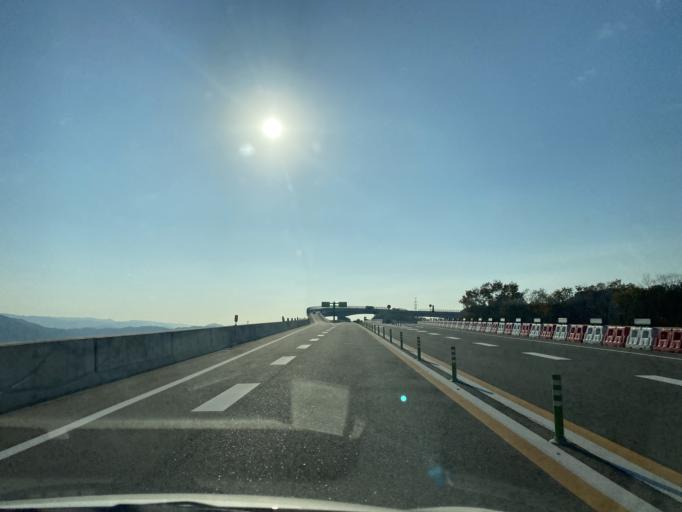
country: JP
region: Wakayama
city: Iwade
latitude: 34.2861
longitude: 135.2774
